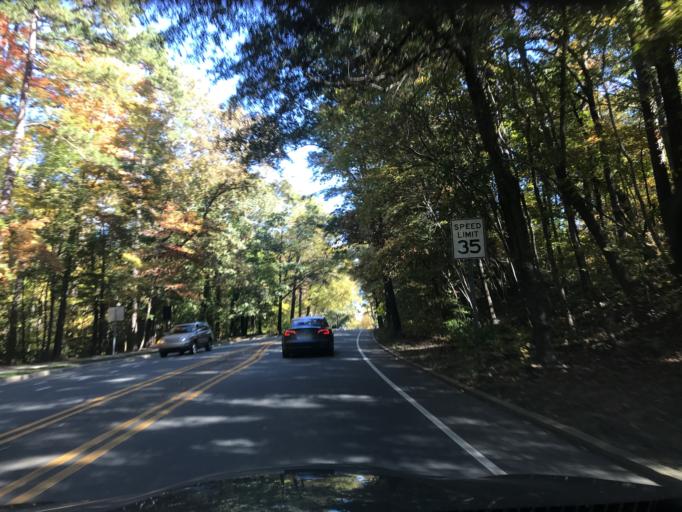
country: US
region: North Carolina
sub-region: Durham County
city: Durham
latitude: 35.9967
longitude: -78.9352
